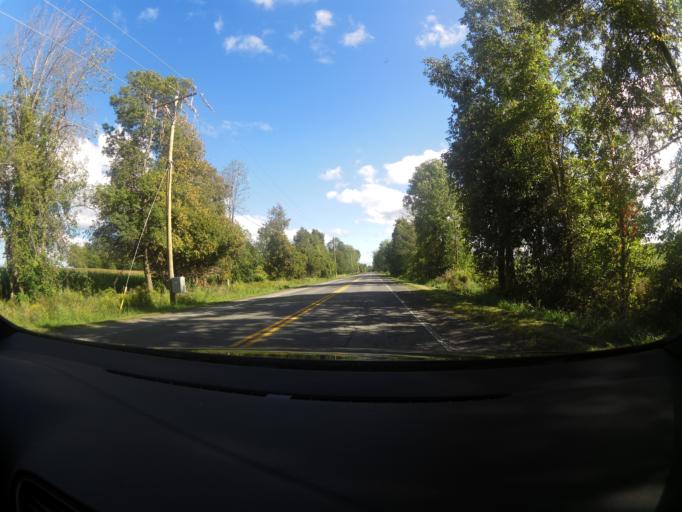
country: CA
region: Ontario
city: Carleton Place
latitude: 45.1462
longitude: -76.0859
